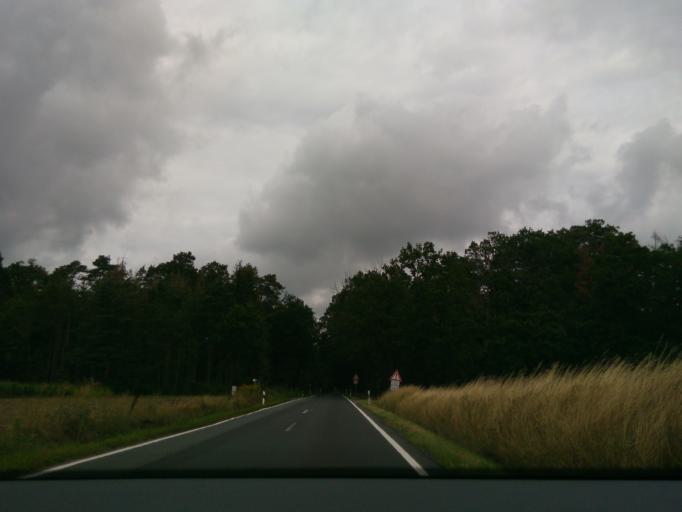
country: DE
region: Bavaria
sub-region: Regierungsbezirk Mittelfranken
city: Weisendorf
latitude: 49.6606
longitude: 10.8086
